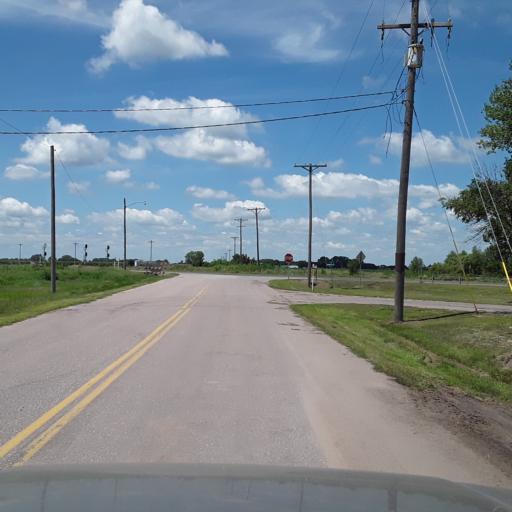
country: US
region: Nebraska
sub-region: Merrick County
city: Central City
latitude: 41.1048
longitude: -98.0200
